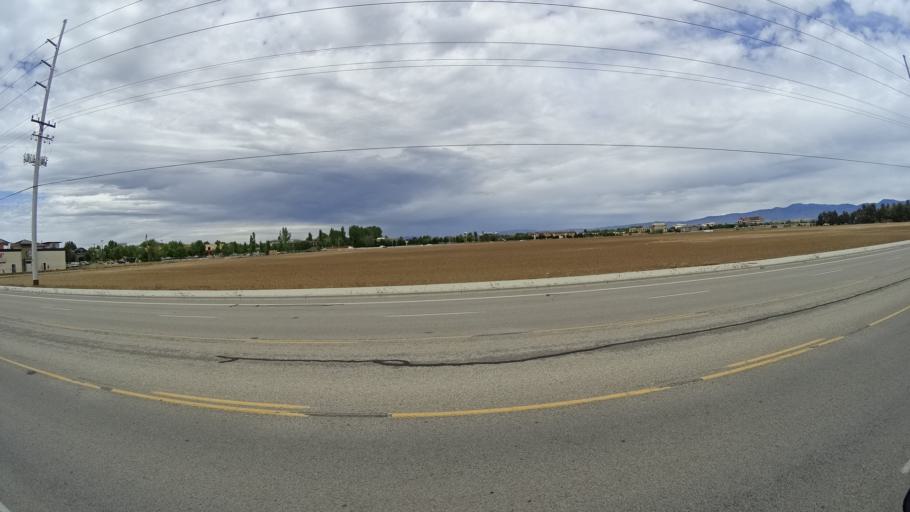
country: US
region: Idaho
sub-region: Ada County
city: Meridian
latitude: 43.5903
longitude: -116.3634
